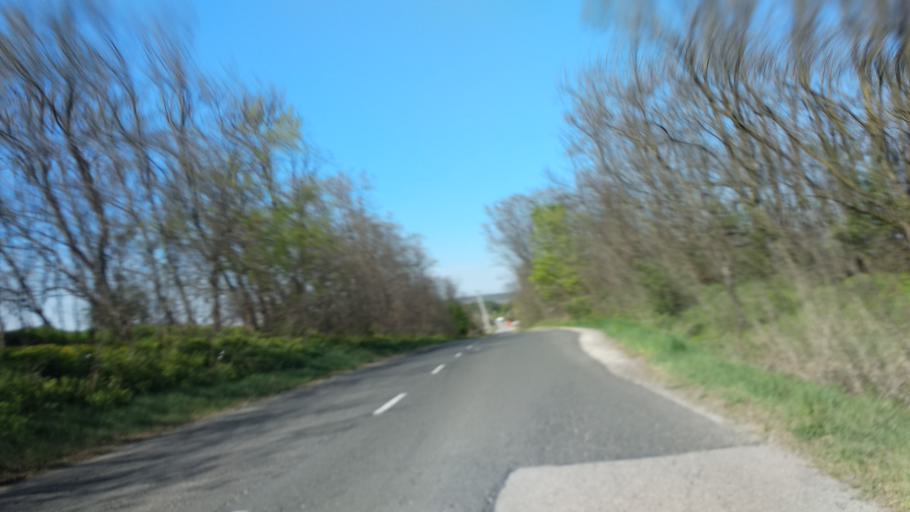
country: HU
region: Pest
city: Godollo
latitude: 47.5838
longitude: 19.3418
